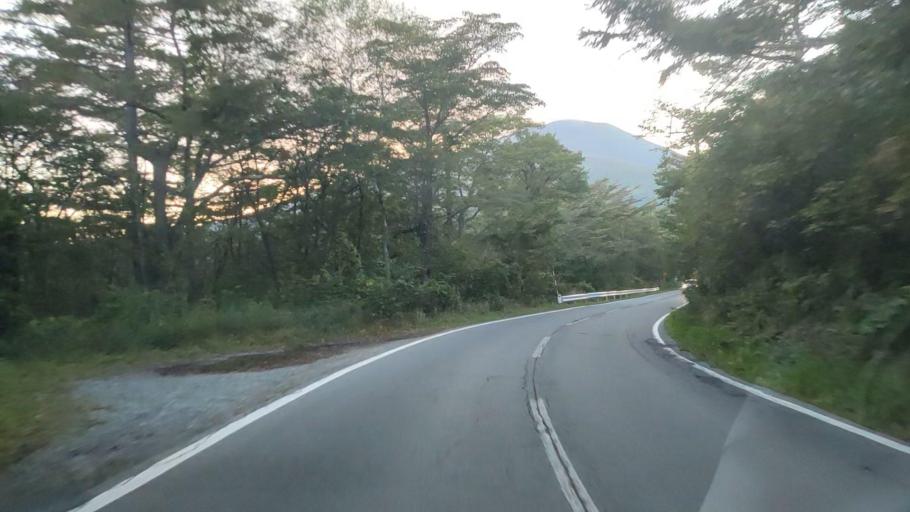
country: JP
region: Nagano
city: Komoro
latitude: 36.3986
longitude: 138.5760
